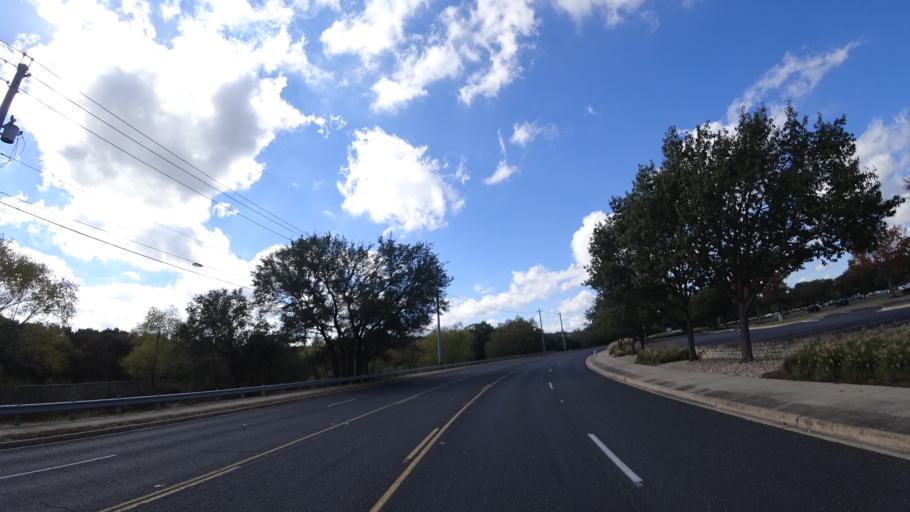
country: US
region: Texas
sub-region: Williamson County
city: Jollyville
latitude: 30.4311
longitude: -97.7343
